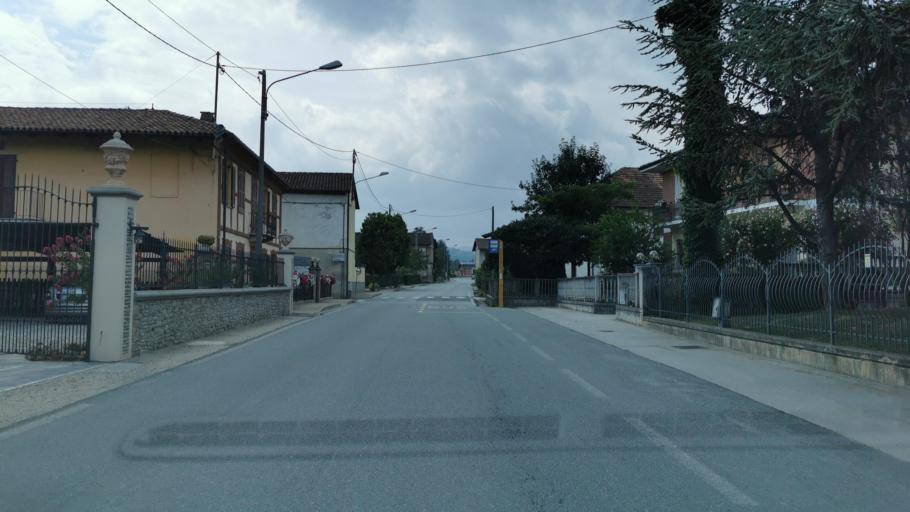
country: IT
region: Piedmont
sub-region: Provincia di Cuneo
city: Grinzane Cavour
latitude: 44.6439
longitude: 7.9992
